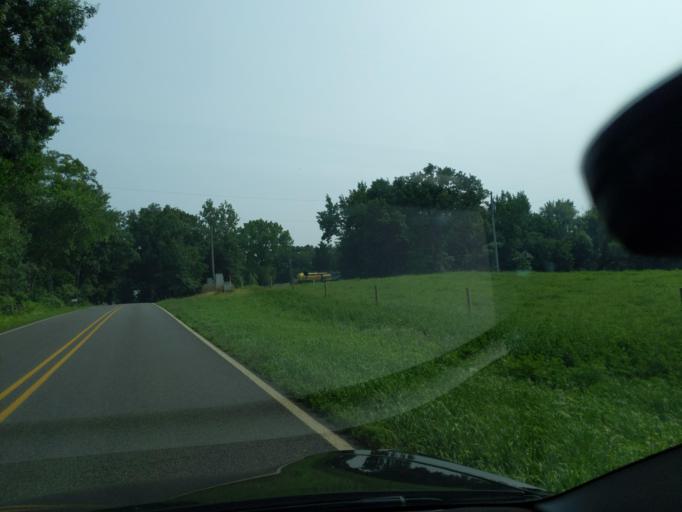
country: US
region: Michigan
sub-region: Ingham County
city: Leslie
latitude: 42.4088
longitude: -84.5611
